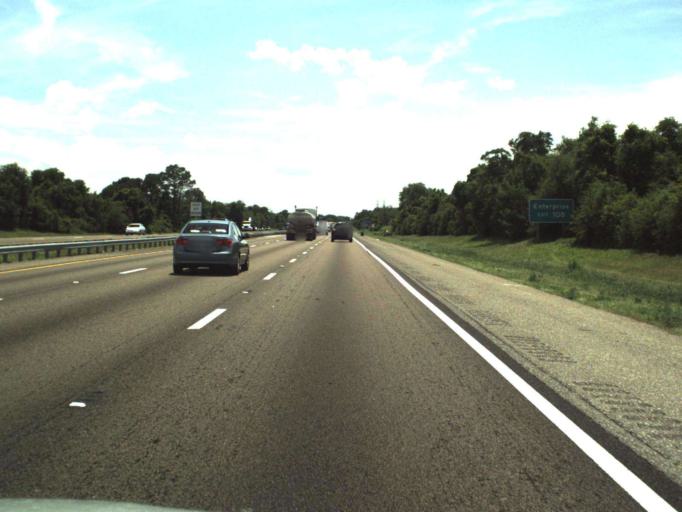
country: US
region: Florida
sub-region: Volusia County
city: Deltona
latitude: 28.8863
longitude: -81.2798
